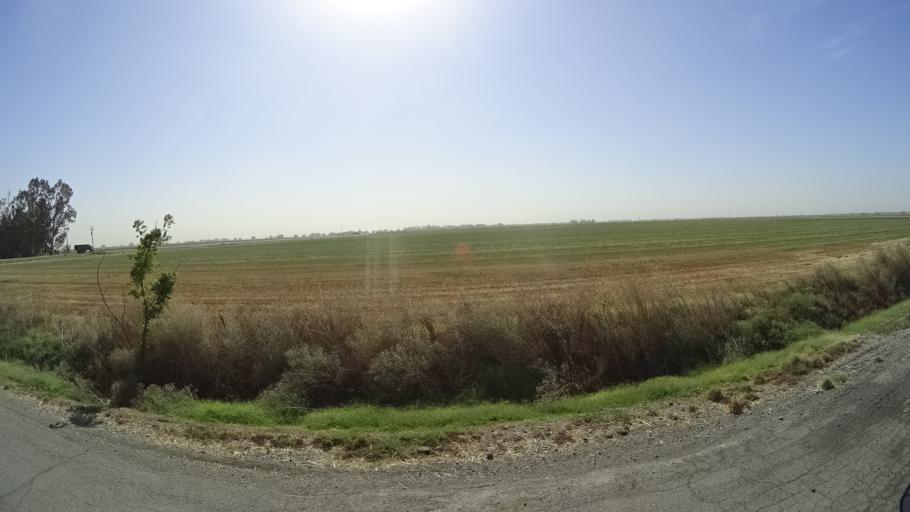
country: US
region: California
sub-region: Yolo County
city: Davis
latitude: 38.5748
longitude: -121.6766
